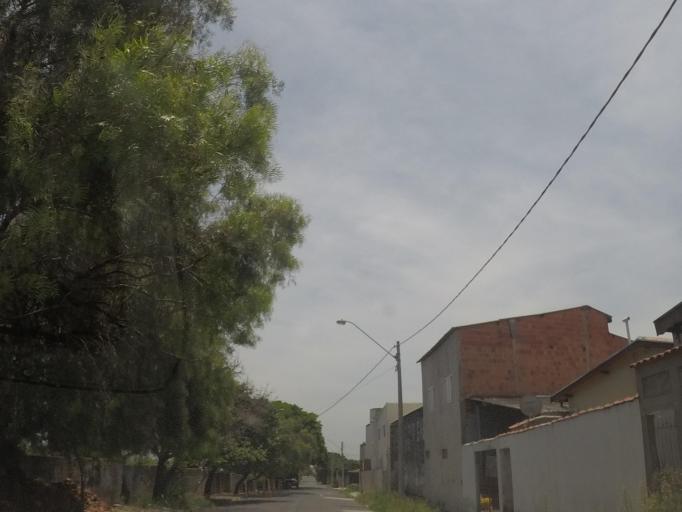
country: BR
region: Sao Paulo
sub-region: Hortolandia
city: Hortolandia
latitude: -22.8596
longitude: -47.1826
